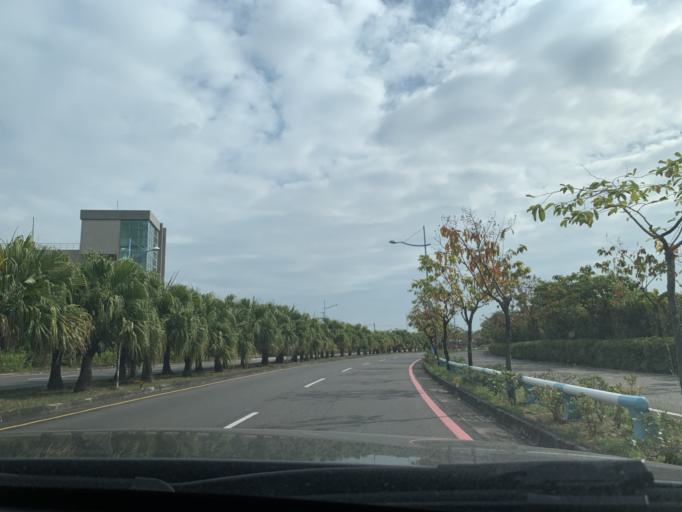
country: TW
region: Taiwan
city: Fengshan
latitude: 22.4528
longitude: 120.4875
